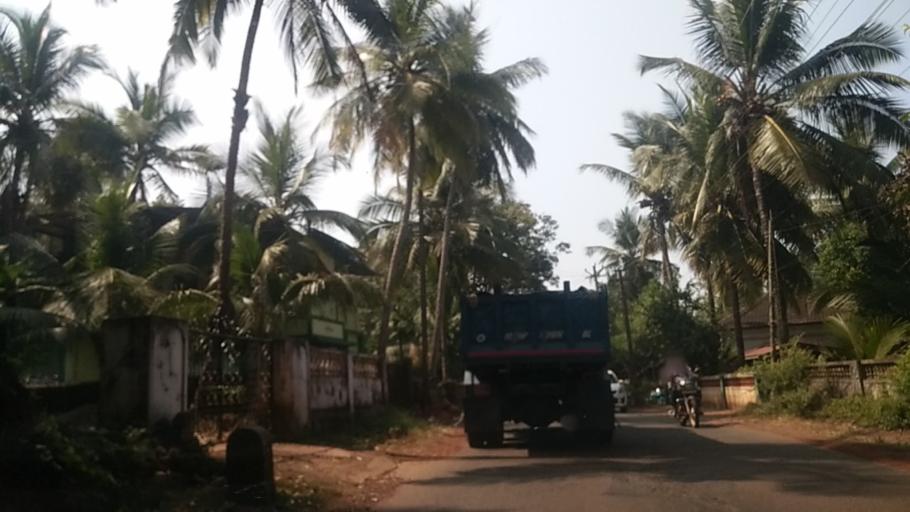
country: IN
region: Goa
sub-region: North Goa
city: Solim
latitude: 15.6144
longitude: 73.7785
